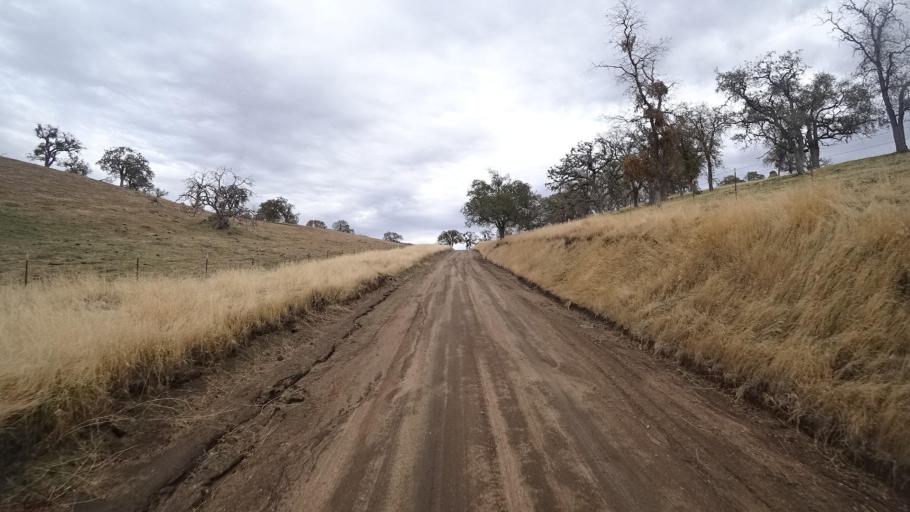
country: US
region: California
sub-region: Kern County
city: Stallion Springs
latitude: 35.1226
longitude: -118.7164
